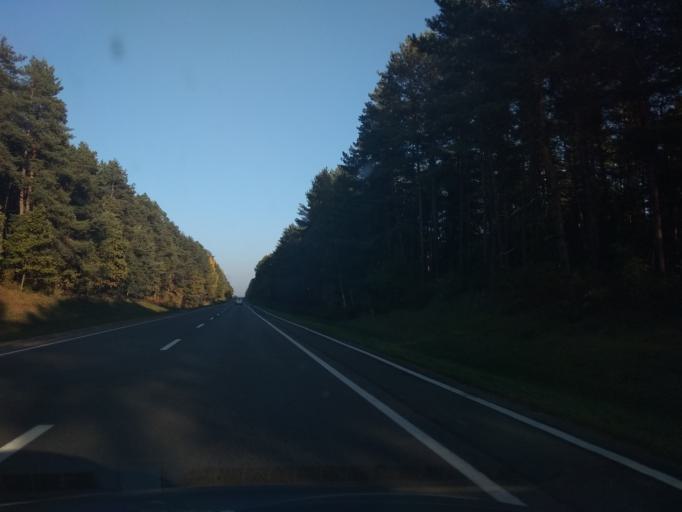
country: BY
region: Grodnenskaya
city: Vawkavysk
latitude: 53.1452
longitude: 24.3701
